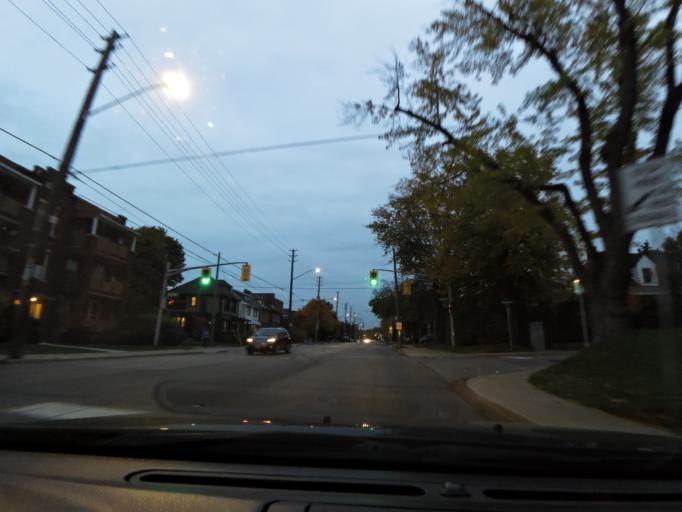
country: CA
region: Ontario
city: Hamilton
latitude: 43.2520
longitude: -79.8969
